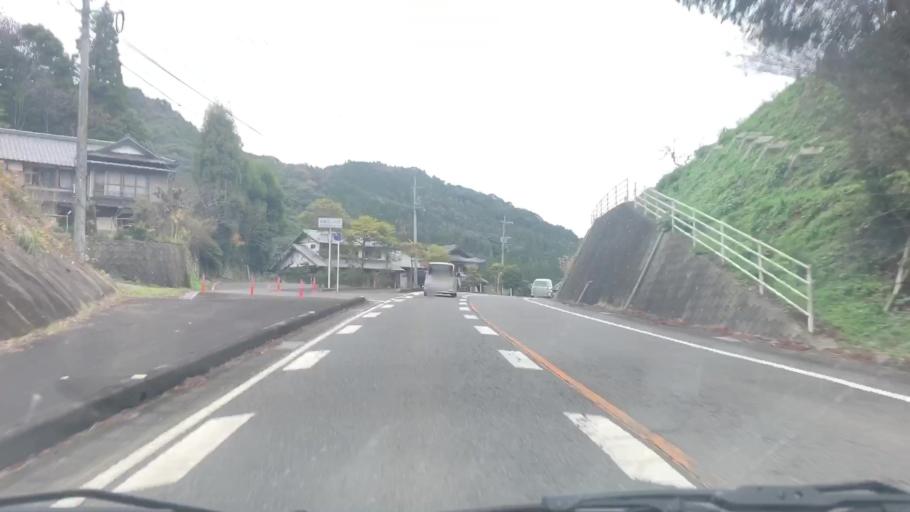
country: JP
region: Saga Prefecture
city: Takeocho-takeo
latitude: 33.1637
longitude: 129.9680
